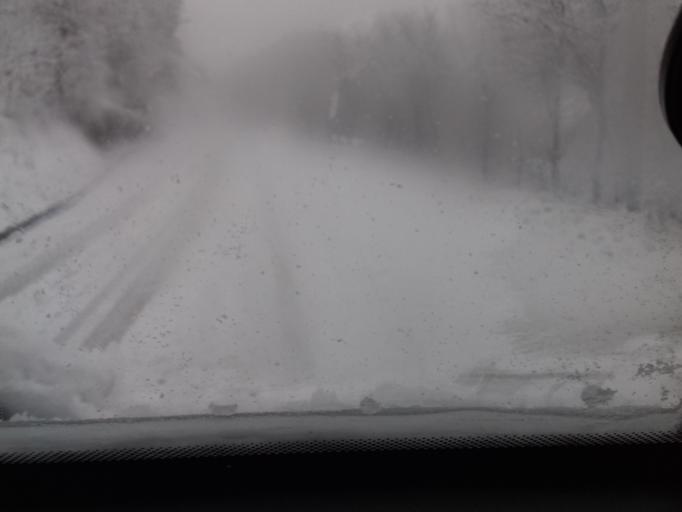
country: BA
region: Federation of Bosnia and Herzegovina
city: Lokvine
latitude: 44.2336
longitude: 17.8266
